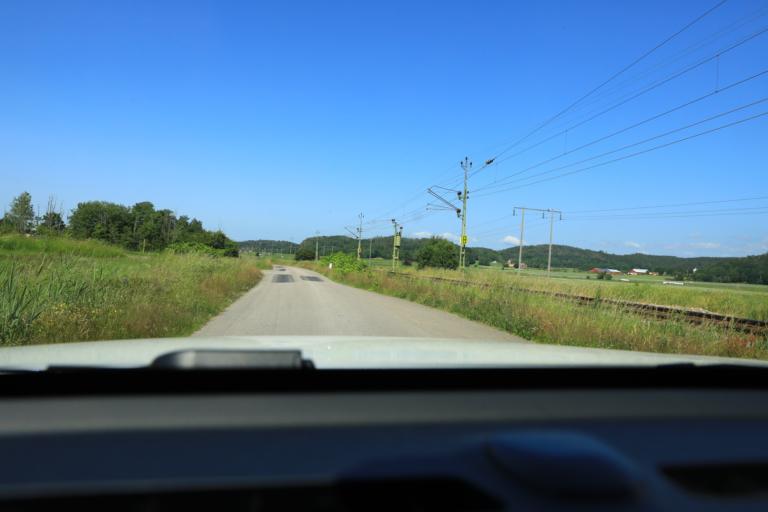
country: SE
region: Halland
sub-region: Varbergs Kommun
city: Varberg
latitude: 57.1775
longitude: 12.3030
